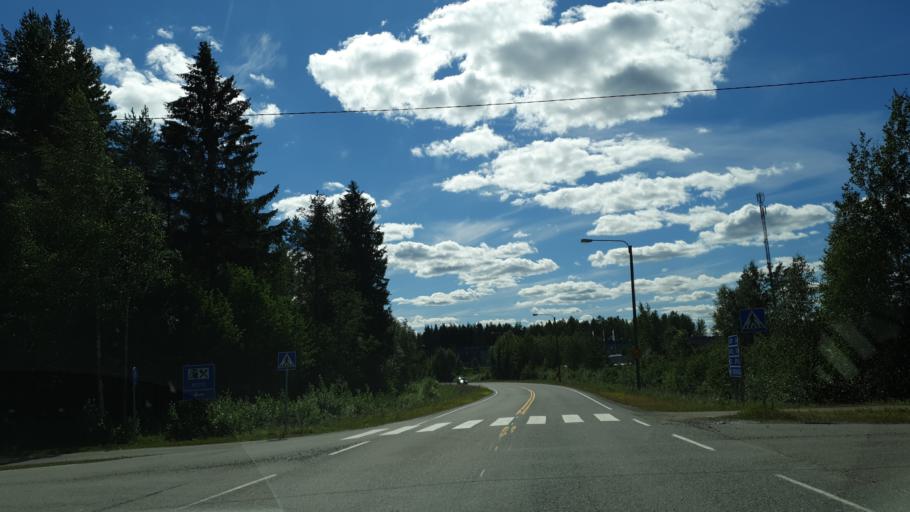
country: FI
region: Northern Savo
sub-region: Varkaus
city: Leppaevirta
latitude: 62.4951
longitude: 27.7556
